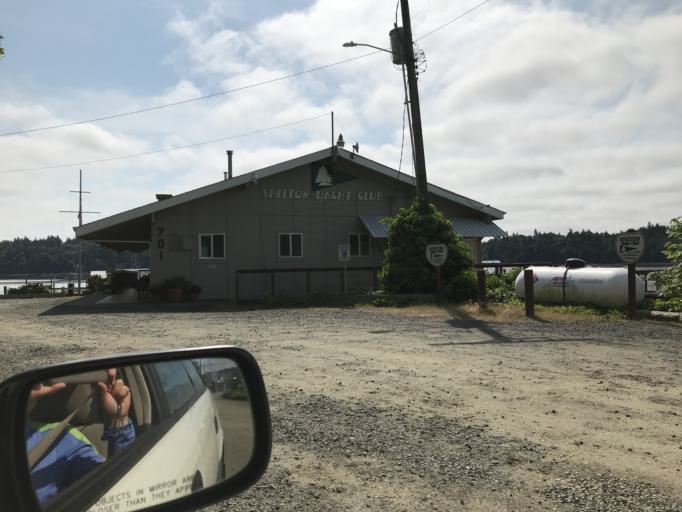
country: US
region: Washington
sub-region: Mason County
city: Shelton
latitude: 47.2145
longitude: -123.0870
